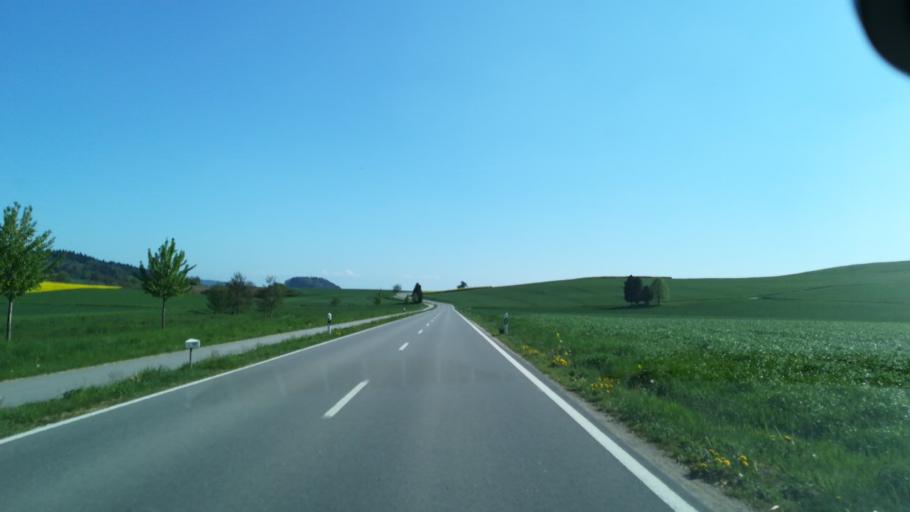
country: DE
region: Baden-Wuerttemberg
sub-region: Freiburg Region
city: Hilzingen
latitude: 47.7872
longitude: 8.7890
